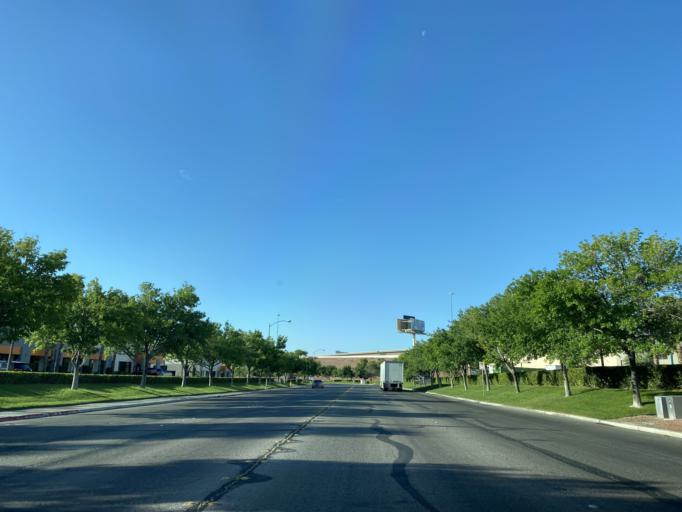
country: US
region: Nevada
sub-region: Clark County
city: Paradise
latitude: 36.0651
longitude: -115.1463
